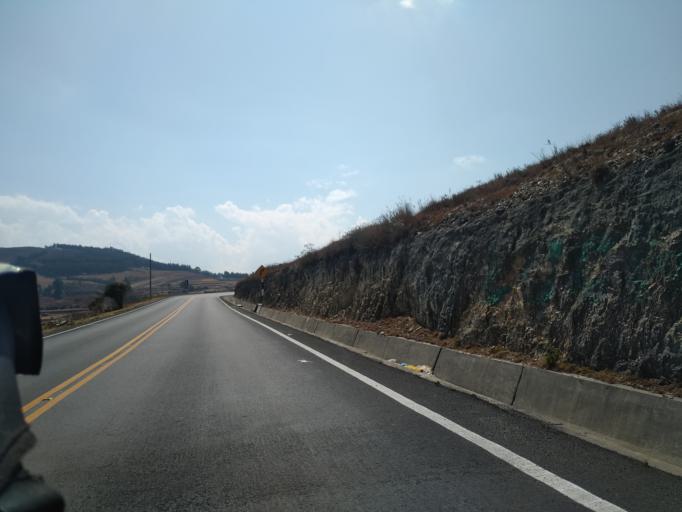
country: PE
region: Cajamarca
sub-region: Provincia de Cajamarca
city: Llacanora
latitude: -7.2066
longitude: -78.3891
